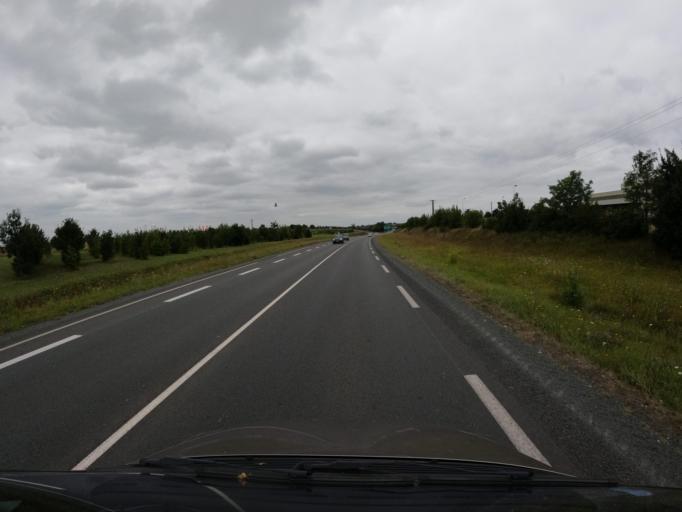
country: FR
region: Pays de la Loire
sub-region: Departement de la Vendee
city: Fontenay-le-Comte
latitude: 46.4453
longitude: -0.8079
